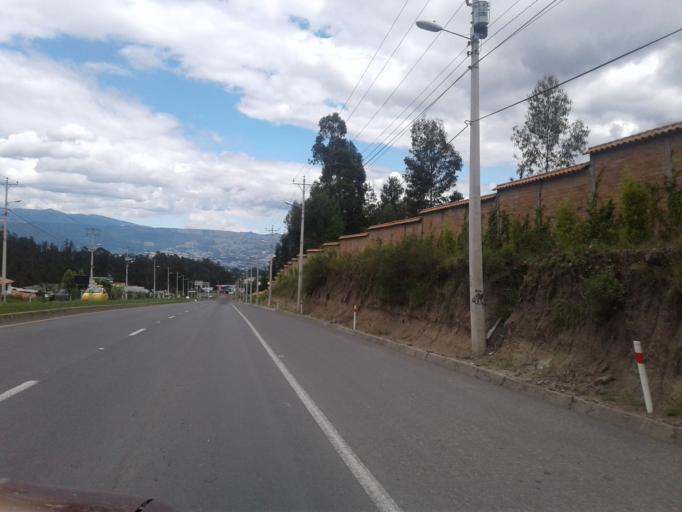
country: EC
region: Pichincha
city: Sangolqui
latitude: -0.3285
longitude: -78.3897
